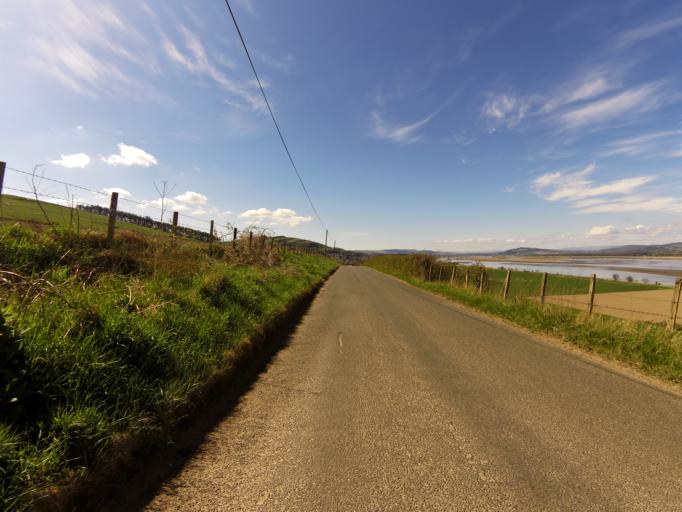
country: GB
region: Scotland
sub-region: Perth and Kinross
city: Errol
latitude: 56.3579
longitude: -3.2027
